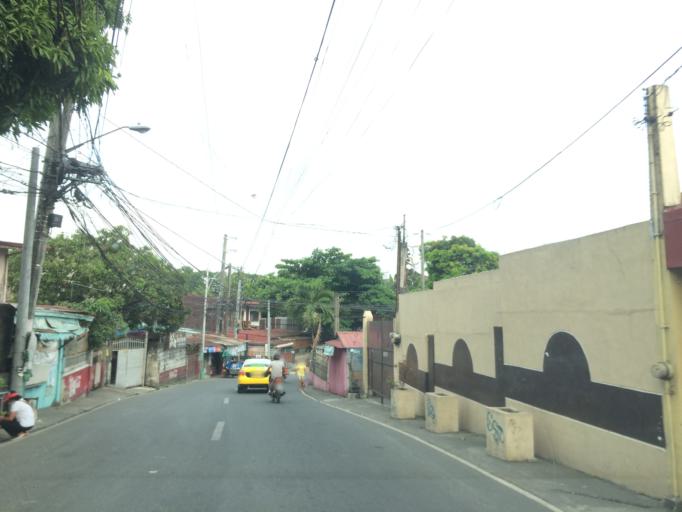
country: PH
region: Calabarzon
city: Bagong Pagasa
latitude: 14.6682
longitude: 121.0168
